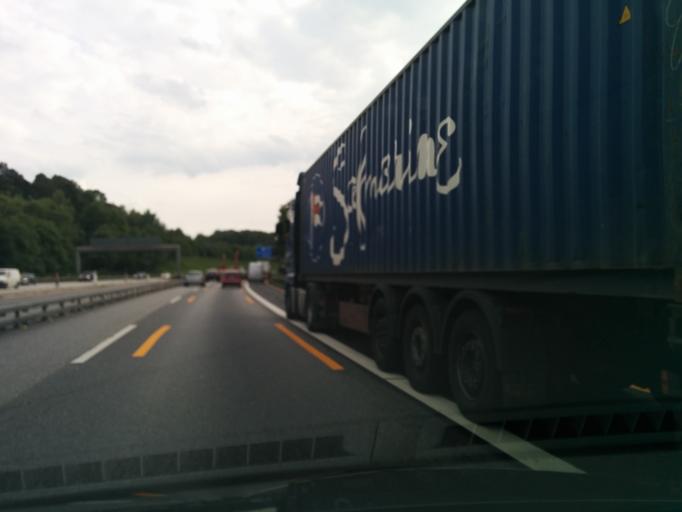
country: DE
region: Hamburg
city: Harburg
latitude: 53.4589
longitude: 9.9280
